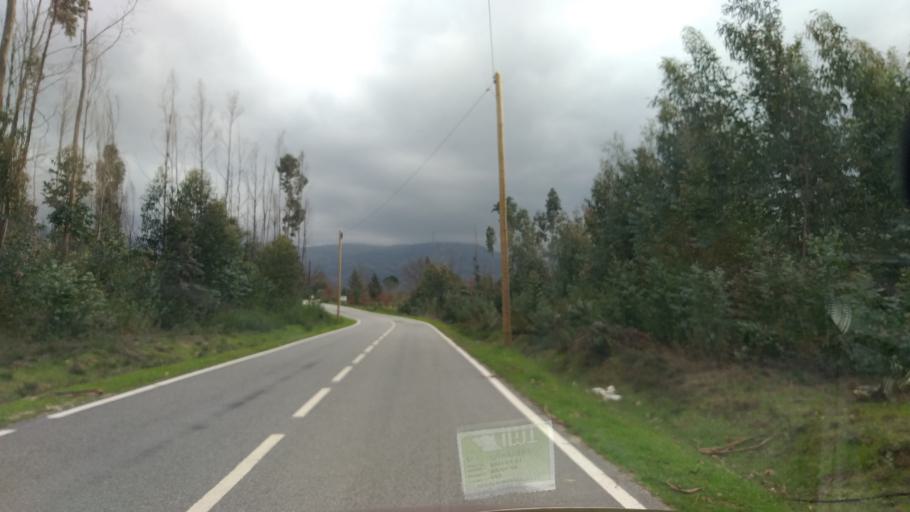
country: PT
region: Guarda
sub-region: Seia
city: Seia
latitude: 40.4814
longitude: -7.6521
